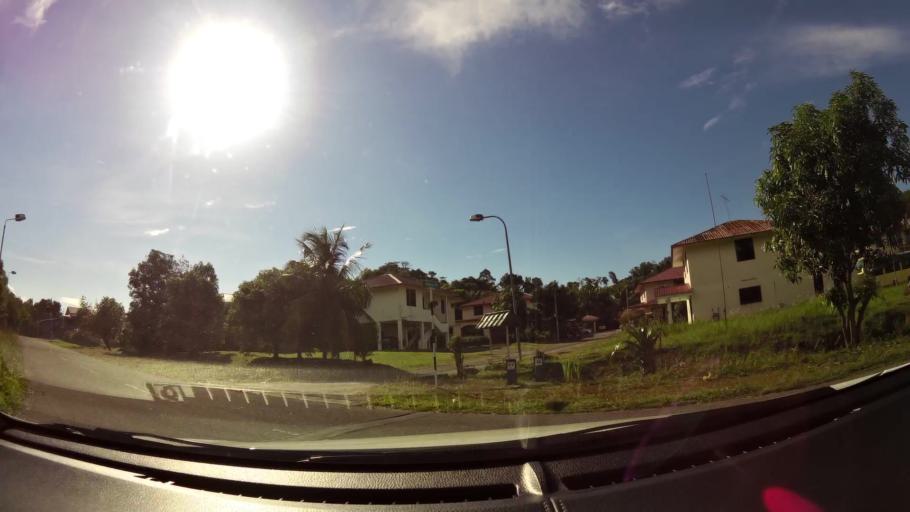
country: BN
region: Brunei and Muara
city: Bandar Seri Begawan
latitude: 4.9647
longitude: 114.9577
